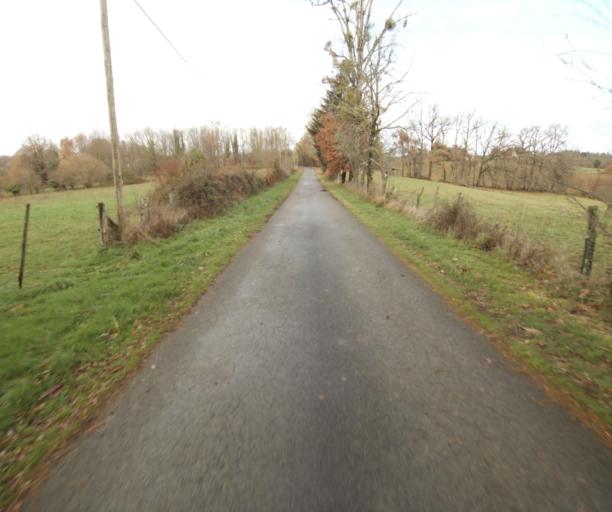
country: FR
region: Limousin
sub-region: Departement de la Correze
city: Sainte-Fereole
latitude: 45.2649
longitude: 1.6025
